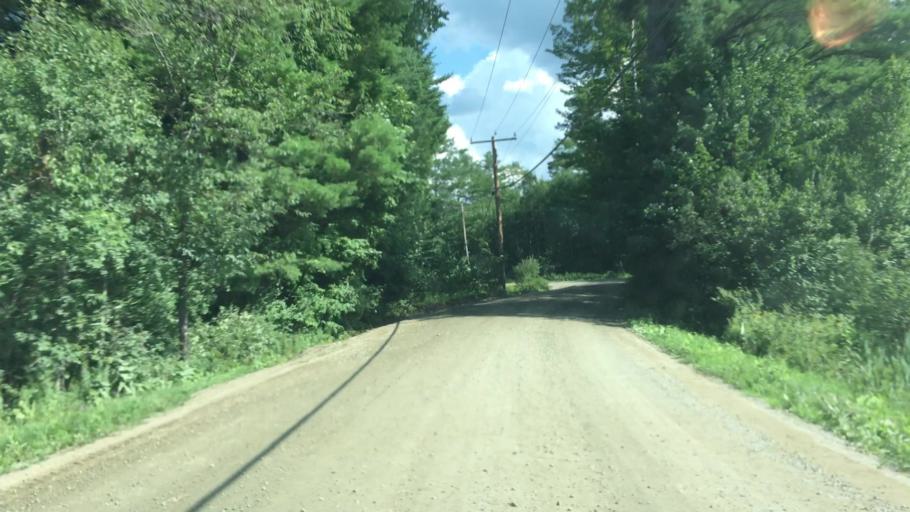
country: US
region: New Hampshire
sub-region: Grafton County
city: North Haverhill
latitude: 44.1306
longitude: -71.9639
